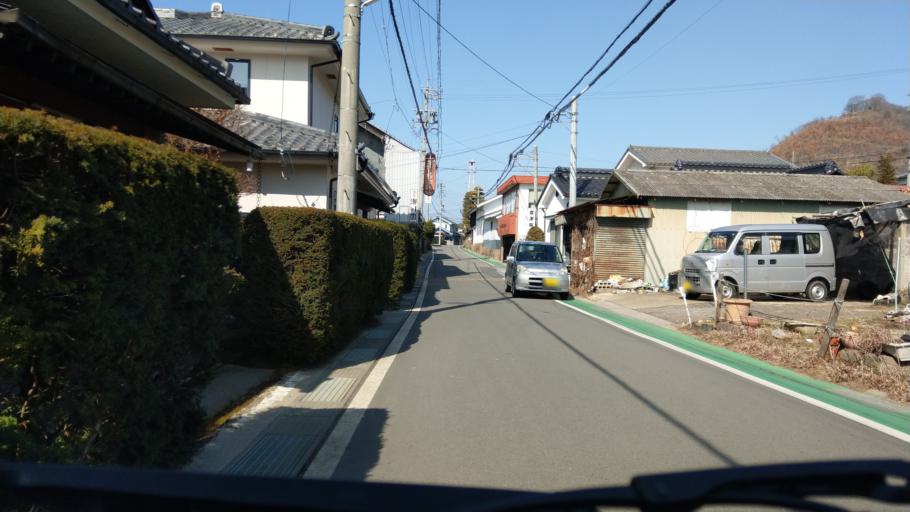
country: JP
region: Nagano
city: Ueda
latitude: 36.3735
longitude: 138.3531
